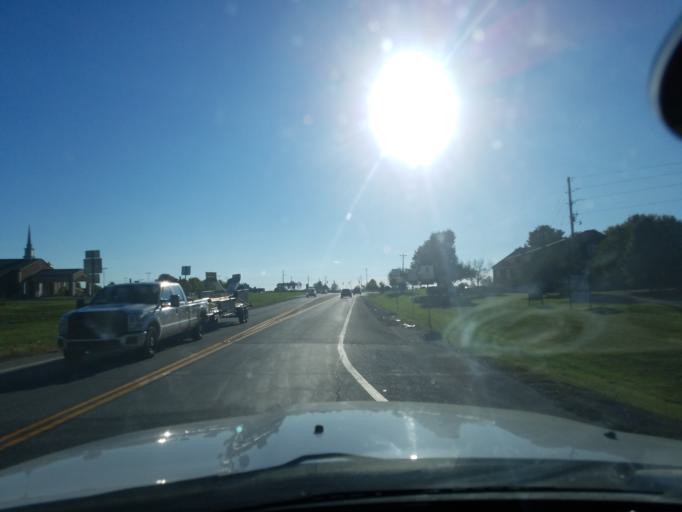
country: US
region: Kentucky
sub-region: Nelson County
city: Bardstown
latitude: 37.7971
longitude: -85.4282
